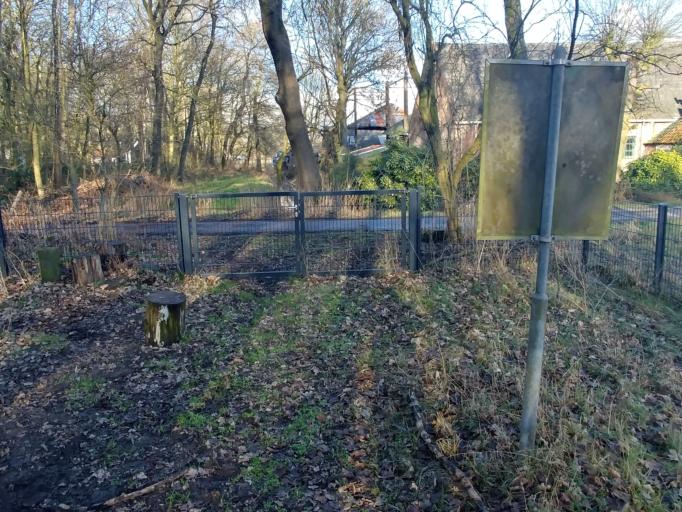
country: NL
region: North Holland
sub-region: Gemeente Bloemendaal
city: Bennebroek
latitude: 52.3438
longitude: 4.5821
